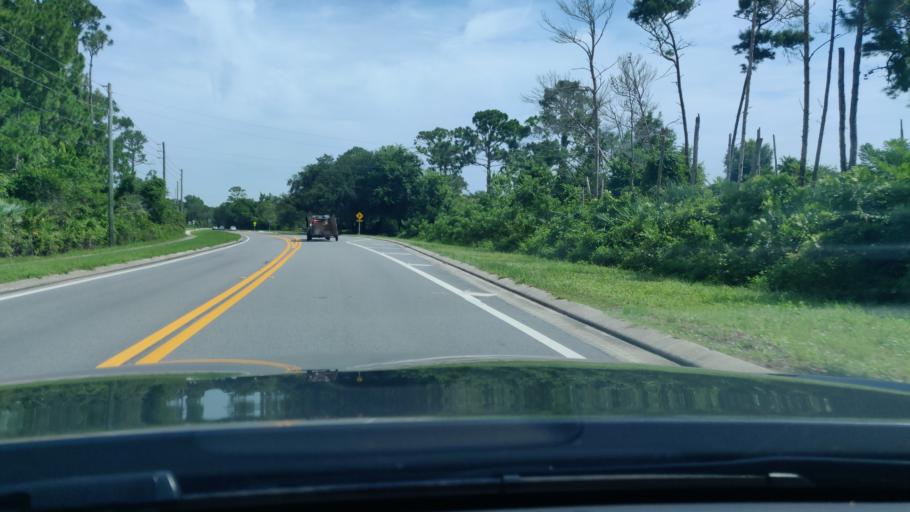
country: US
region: Florida
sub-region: Flagler County
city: Palm Coast
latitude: 29.5445
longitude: -81.1757
